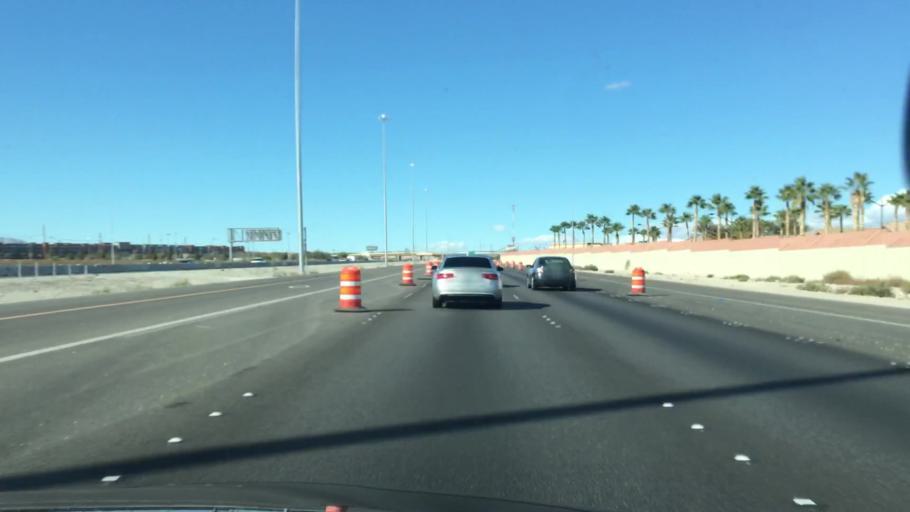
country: US
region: Nevada
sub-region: Clark County
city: Las Vegas
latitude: 36.2845
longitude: -115.2729
